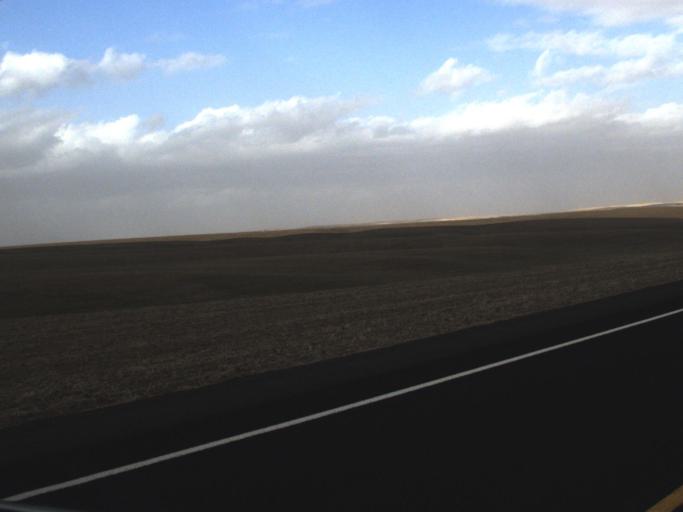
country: US
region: Washington
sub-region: Lincoln County
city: Davenport
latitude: 47.4651
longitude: -118.3003
